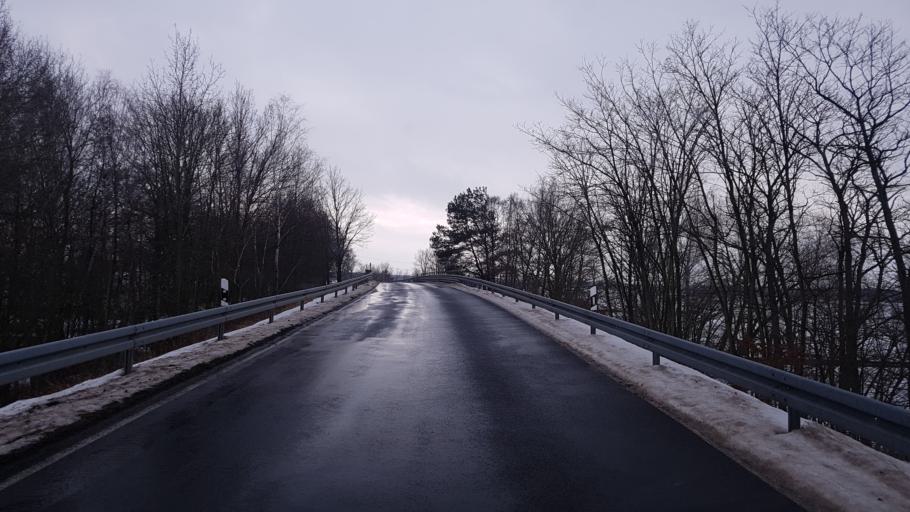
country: DE
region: Brandenburg
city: Bronkow
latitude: 51.6429
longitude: 13.9269
